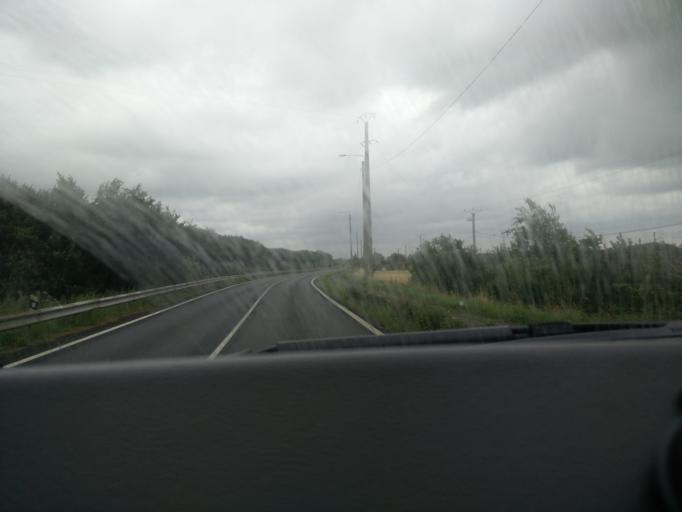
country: FR
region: Nord-Pas-de-Calais
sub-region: Departement du Nord
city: Coudekerque-Village
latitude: 50.9894
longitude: 2.4002
